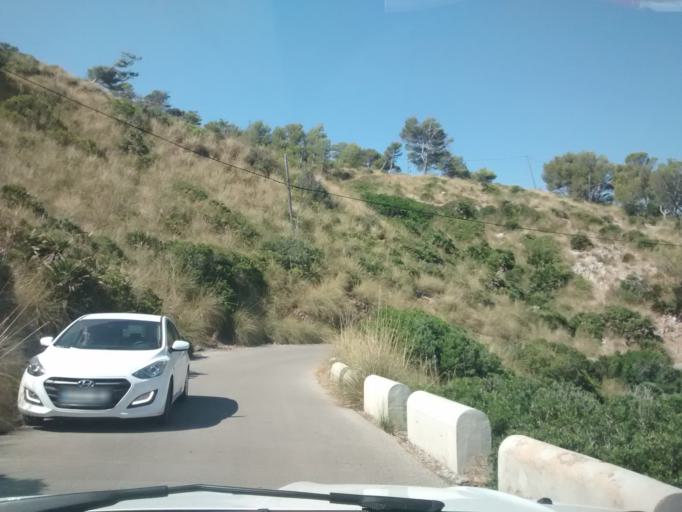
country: ES
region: Balearic Islands
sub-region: Illes Balears
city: Port d'Alcudia
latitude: 39.8751
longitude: 3.1705
